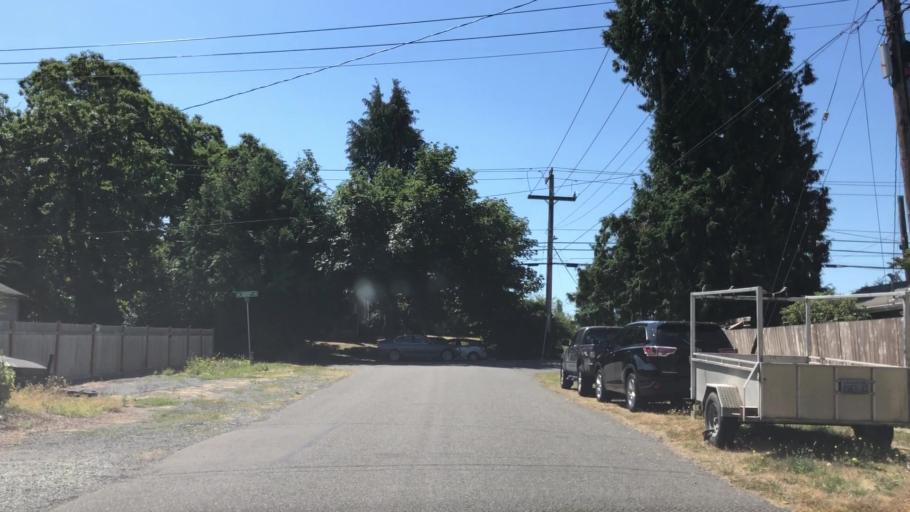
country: US
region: Washington
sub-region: King County
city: Shoreline
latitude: 47.7018
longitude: -122.3375
